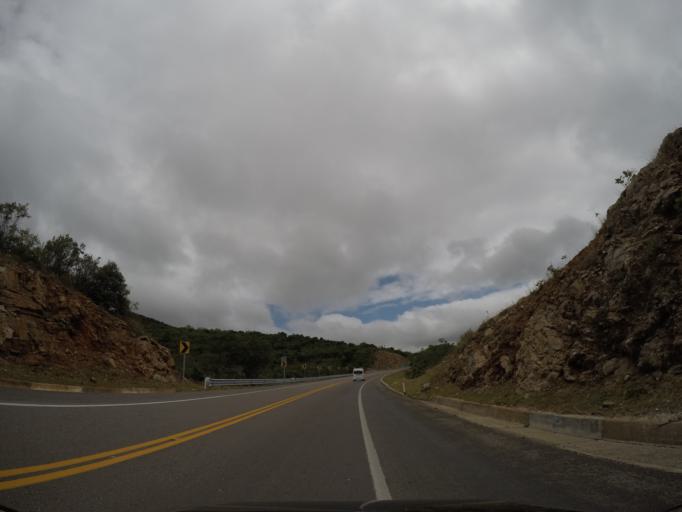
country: MX
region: Oaxaca
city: San Lorenzo Albarradas
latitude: 16.9252
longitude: -96.2584
